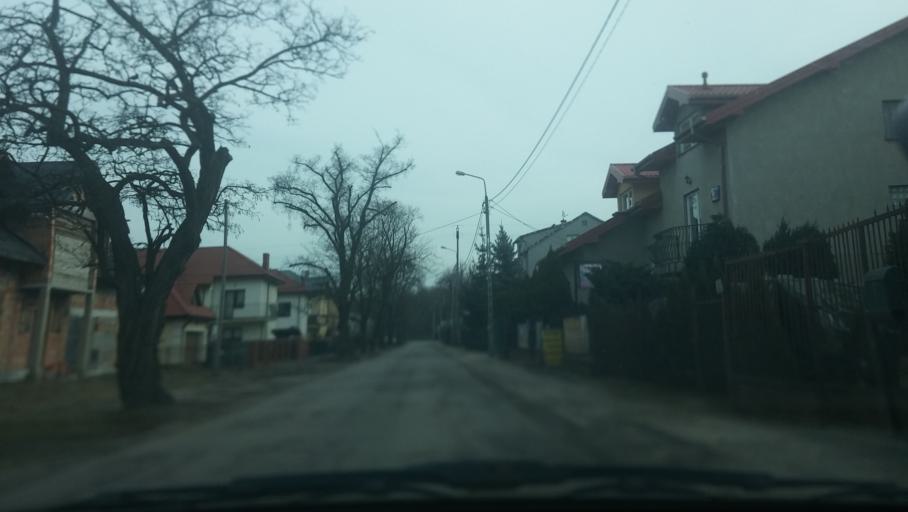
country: PL
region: Masovian Voivodeship
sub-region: Powiat wolominski
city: Zabki
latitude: 52.3045
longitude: 21.1023
